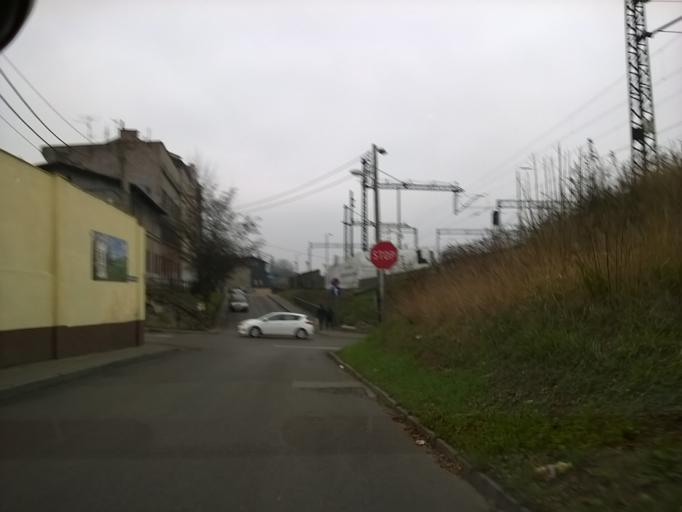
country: PL
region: Silesian Voivodeship
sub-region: Swietochlowice
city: Swietochlowice
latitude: 50.2760
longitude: 18.9489
